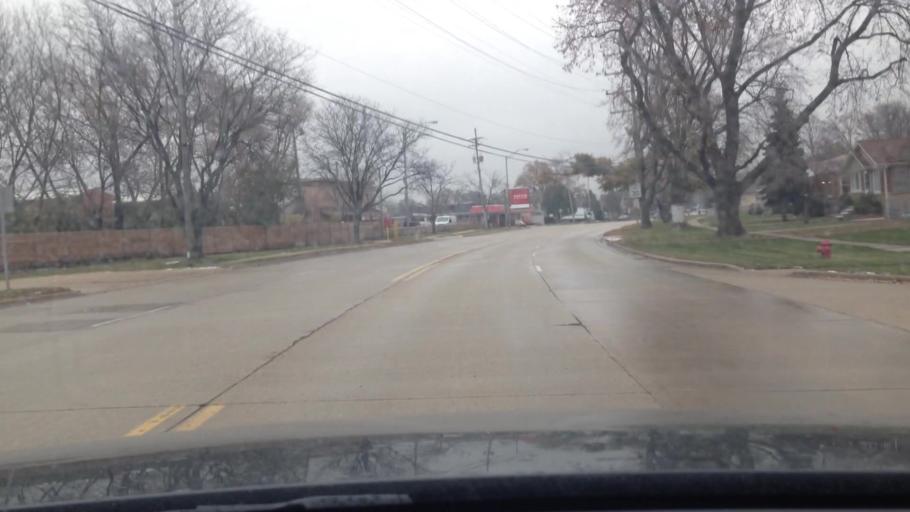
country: US
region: Illinois
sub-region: Cook County
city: Schiller Park
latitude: 41.9600
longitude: -87.8713
